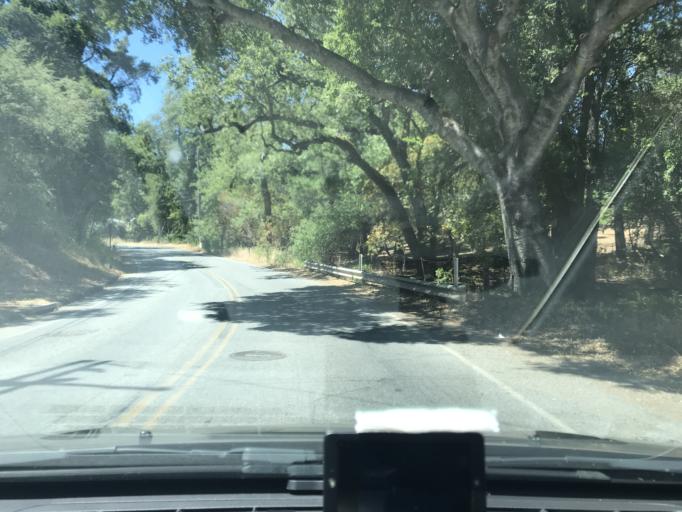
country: US
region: California
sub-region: Santa Clara County
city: Monte Sereno
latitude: 37.2319
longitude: -121.9916
